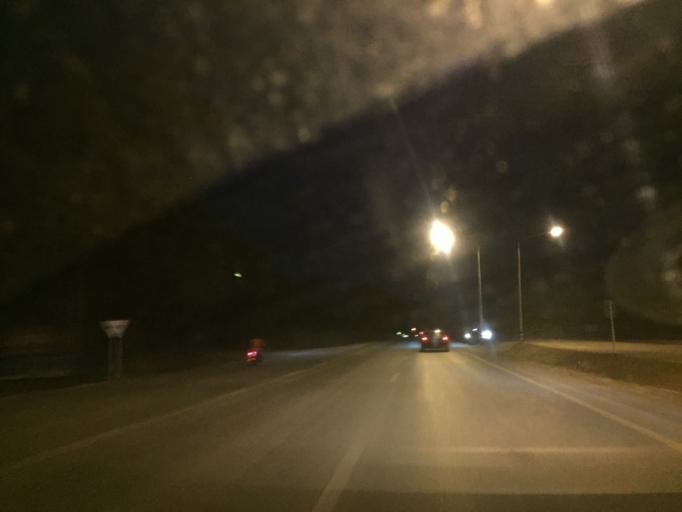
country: TH
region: Changwat Nong Bua Lamphu
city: Na Klang
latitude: 17.2926
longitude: 102.2623
